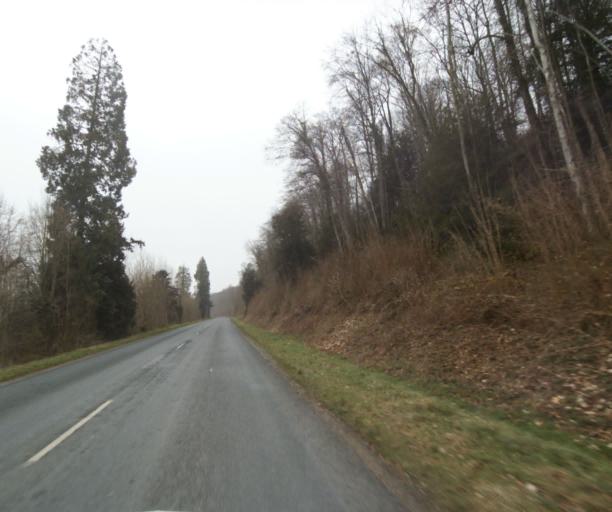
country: FR
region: Champagne-Ardenne
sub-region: Departement de la Haute-Marne
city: Bienville
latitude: 48.5774
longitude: 5.0391
